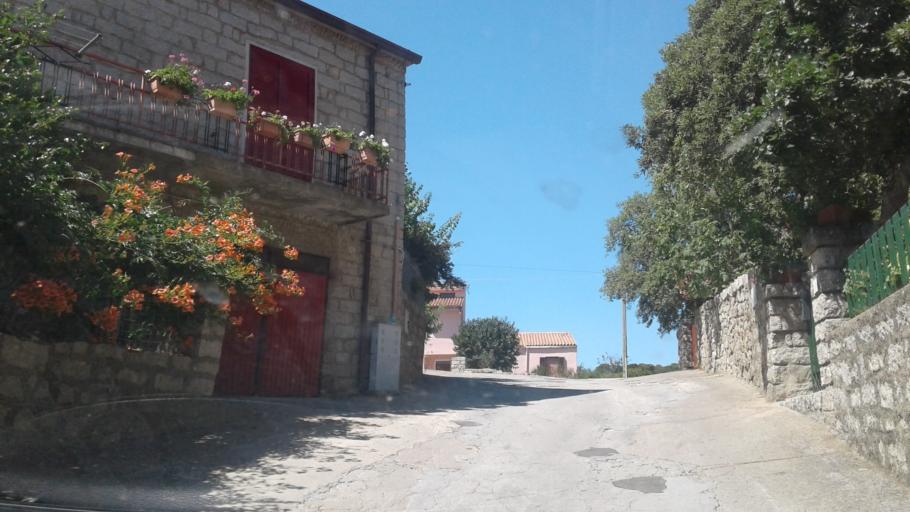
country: IT
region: Sardinia
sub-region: Provincia di Olbia-Tempio
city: Aggius
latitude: 40.9308
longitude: 9.0682
